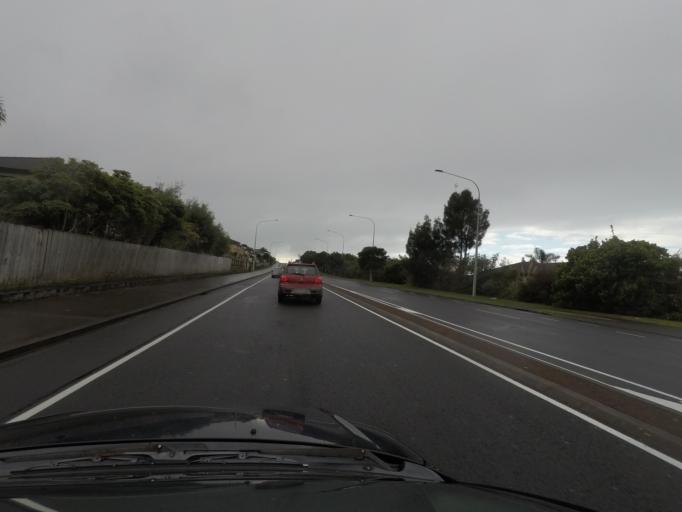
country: NZ
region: Auckland
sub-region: Auckland
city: Rothesay Bay
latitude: -36.7301
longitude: 174.7245
